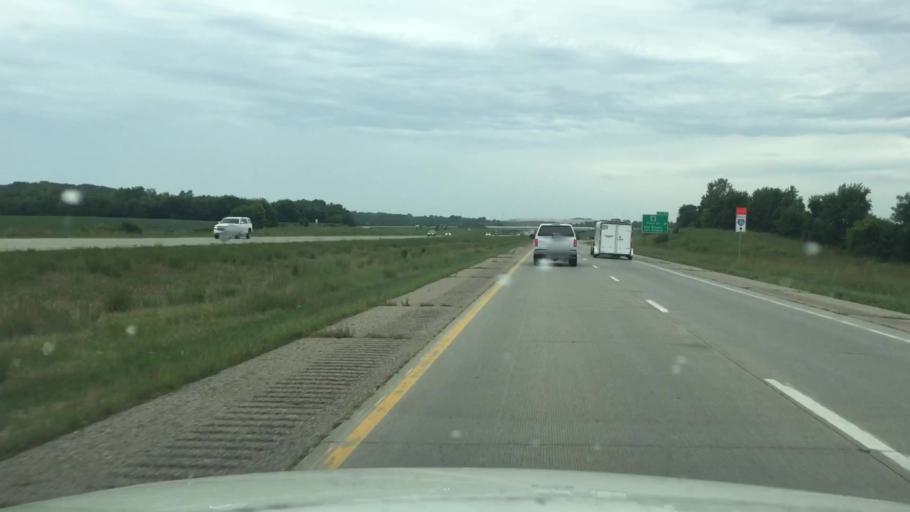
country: US
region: Iowa
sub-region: Warren County
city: Norwalk
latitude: 41.5033
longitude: -93.6355
